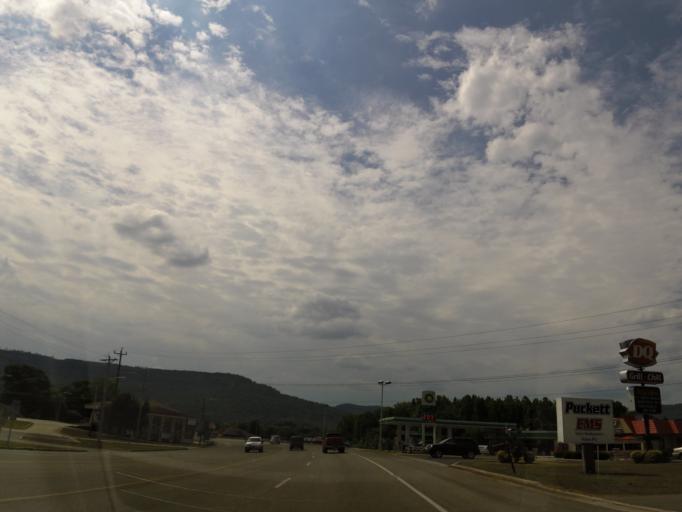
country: US
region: Tennessee
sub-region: Marion County
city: Jasper
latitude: 35.0732
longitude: -85.6158
